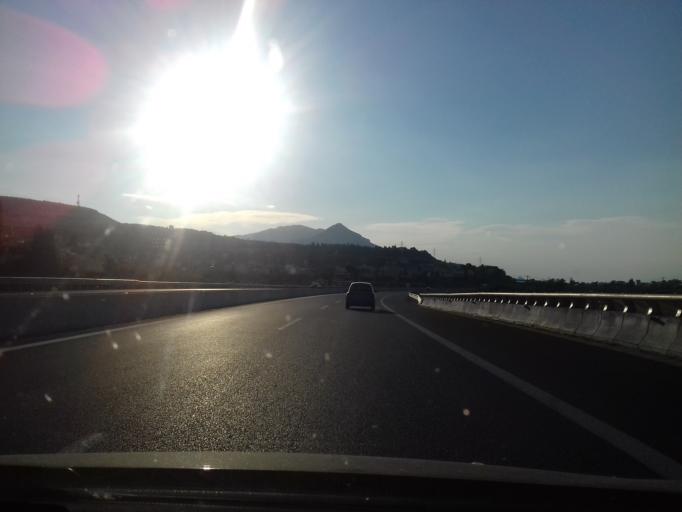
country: GR
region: Peloponnese
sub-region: Nomos Korinthias
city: Xylokastro
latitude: 38.0651
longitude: 22.6495
